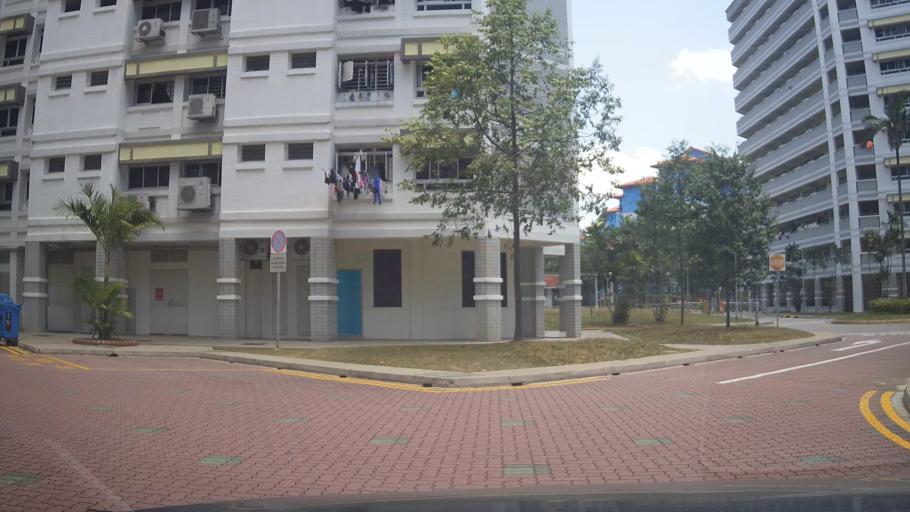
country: MY
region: Johor
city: Kampung Pasir Gudang Baru
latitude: 1.3685
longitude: 103.9612
